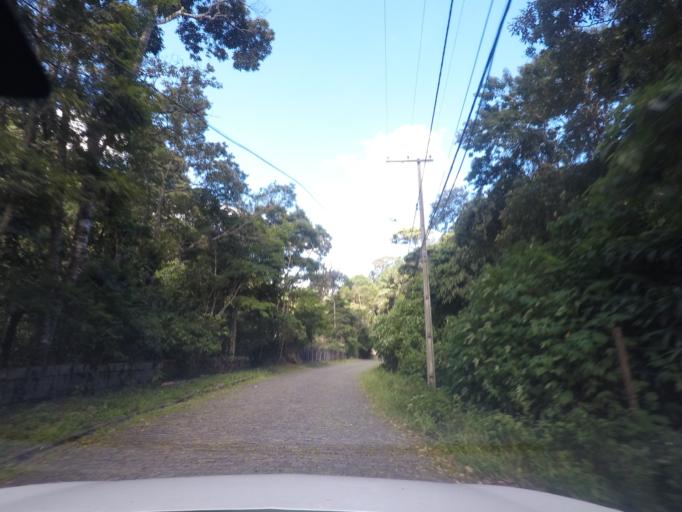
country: BR
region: Rio de Janeiro
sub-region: Teresopolis
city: Teresopolis
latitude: -22.4334
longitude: -42.9932
